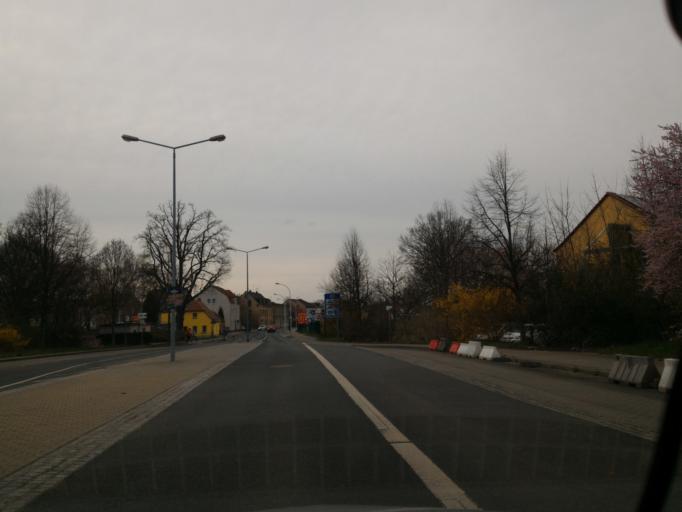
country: DE
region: Saxony
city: Zittau
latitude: 50.8841
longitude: 14.8182
